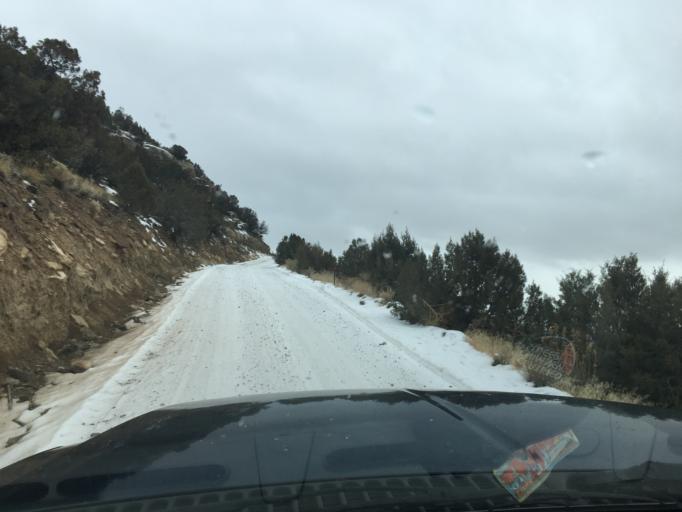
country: US
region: Colorado
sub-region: Garfield County
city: Parachute
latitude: 39.3488
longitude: -108.1732
